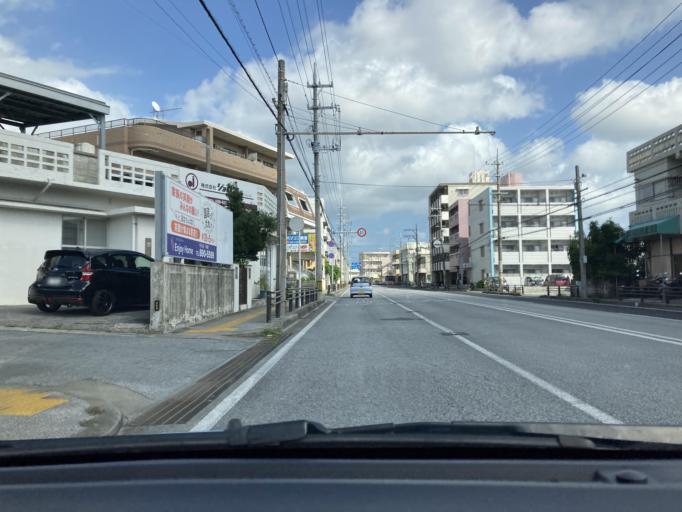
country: JP
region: Okinawa
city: Tomigusuku
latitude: 26.1961
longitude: 127.6998
